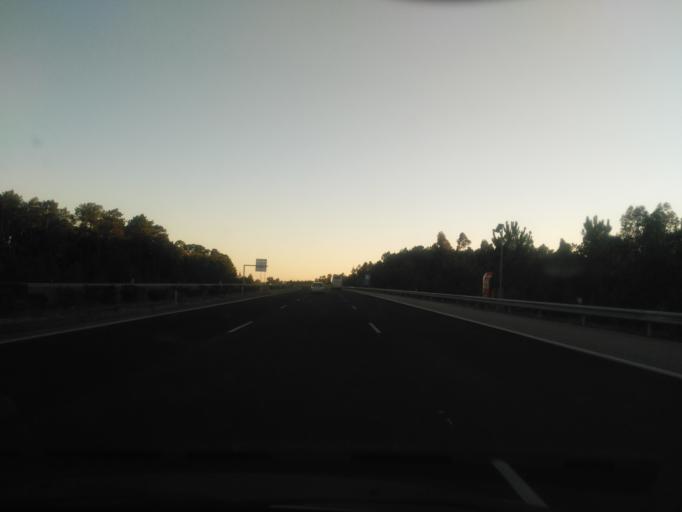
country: PT
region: Leiria
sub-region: Leiria
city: Maceira
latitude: 39.6947
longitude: -8.9282
